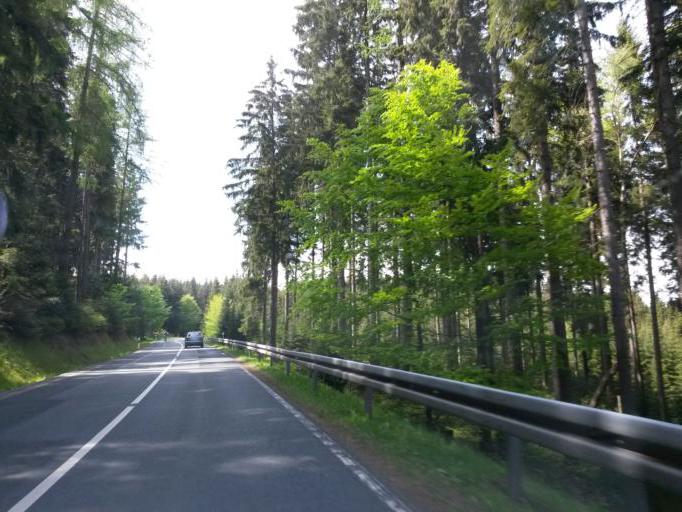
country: DE
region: Saxony
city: Zwota
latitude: 50.3613
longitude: 12.4186
